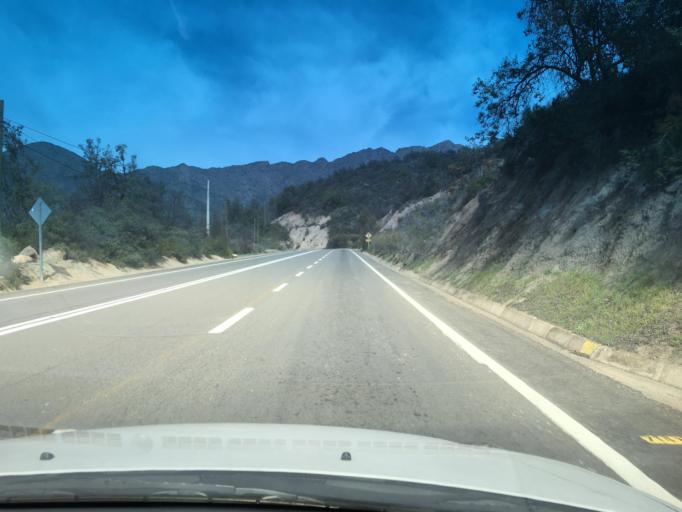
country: CL
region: Valparaiso
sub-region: Provincia de San Felipe
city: Llaillay
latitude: -33.0630
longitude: -70.9883
